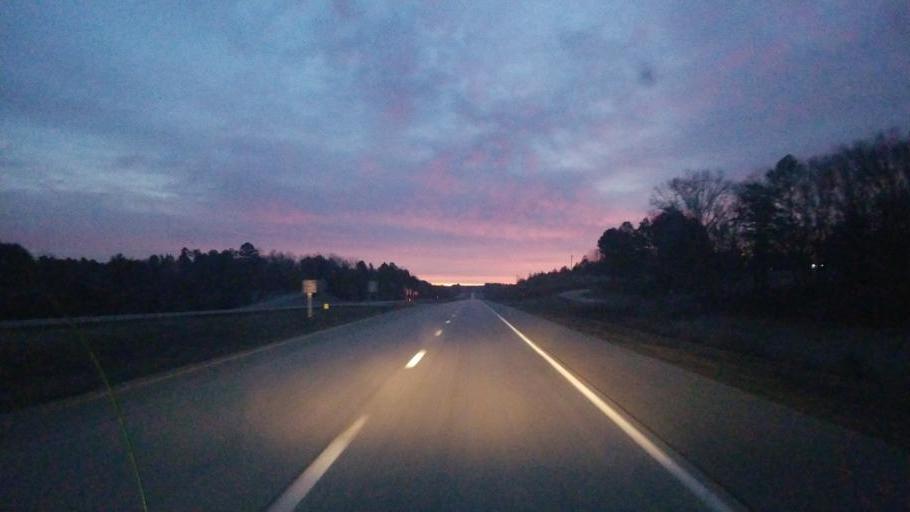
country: US
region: Missouri
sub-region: Shannon County
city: Winona
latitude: 36.9969
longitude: -91.4506
